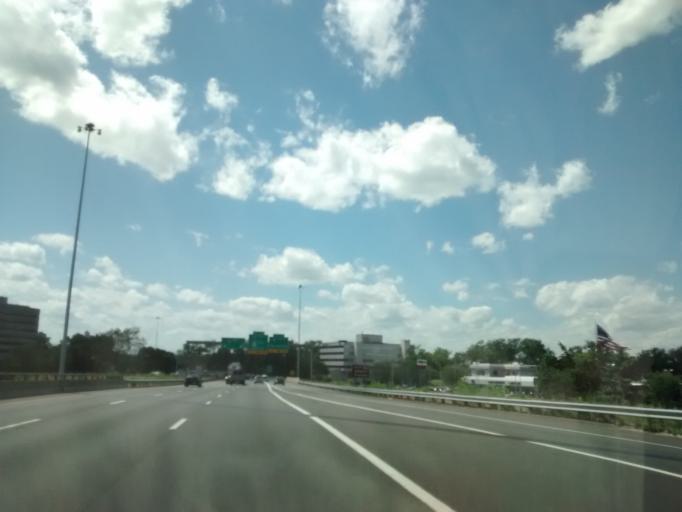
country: US
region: Connecticut
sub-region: Hartford County
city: Hartford
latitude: 41.7683
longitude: -72.6582
